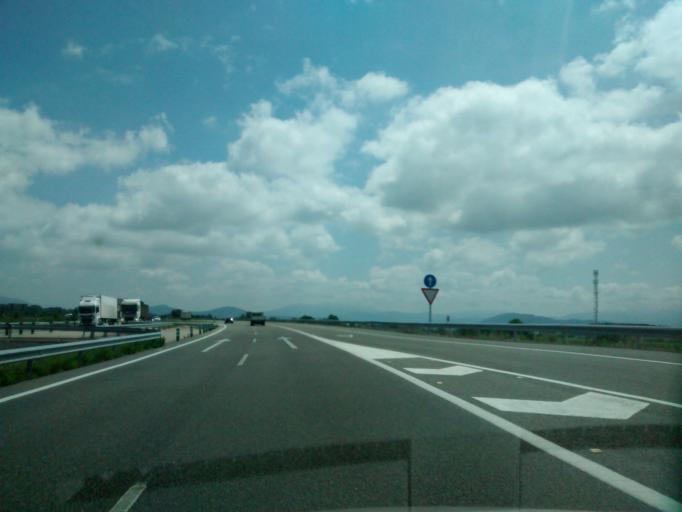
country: ES
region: Castille and Leon
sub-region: Provincia de Leon
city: Carracedelo
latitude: 42.5663
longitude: -6.7266
